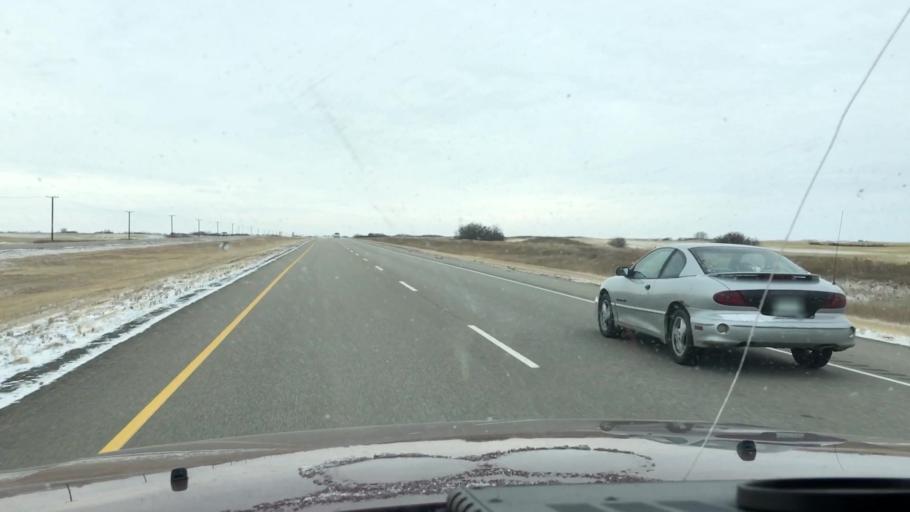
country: CA
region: Saskatchewan
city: Watrous
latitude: 51.4062
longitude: -106.1818
